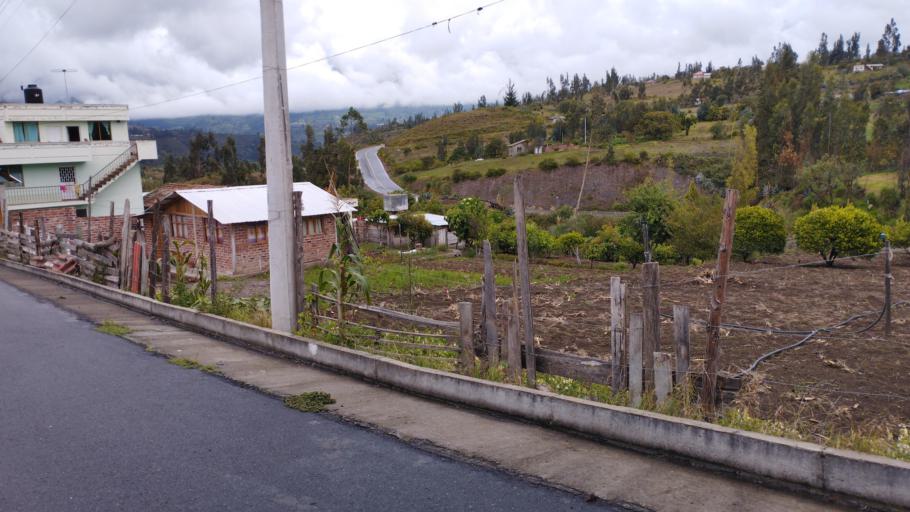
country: EC
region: Chimborazo
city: Guano
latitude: -1.6218
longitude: -78.6107
